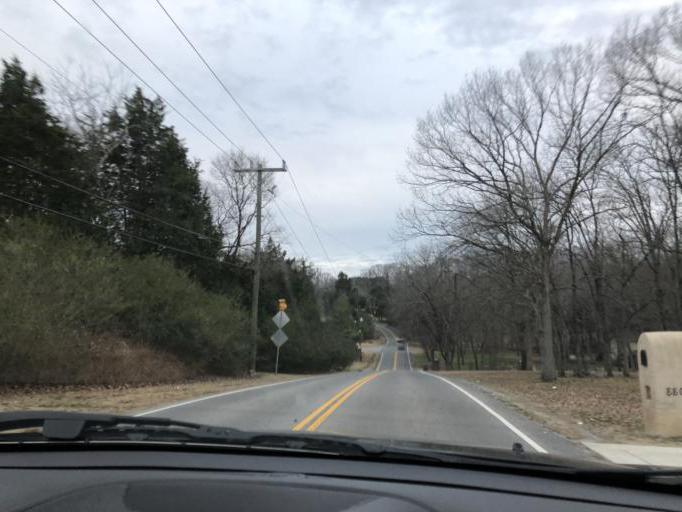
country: US
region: Tennessee
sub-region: Wilson County
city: Green Hill
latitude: 36.1941
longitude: -86.5913
